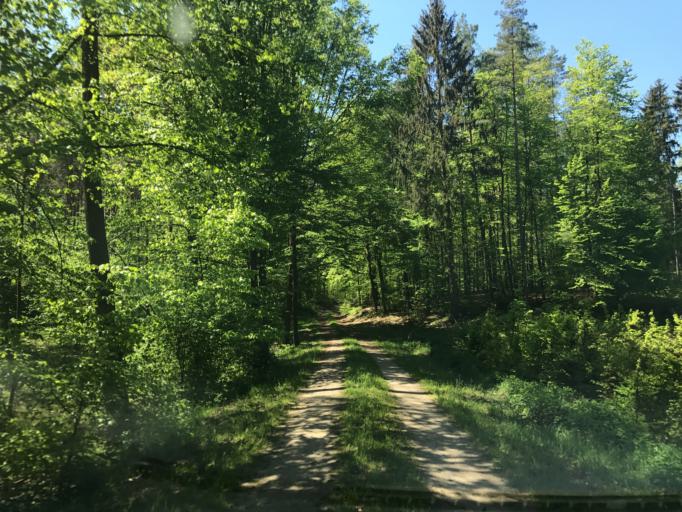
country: PL
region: Kujawsko-Pomorskie
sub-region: Powiat brodnicki
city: Gorzno
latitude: 53.2121
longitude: 19.7183
